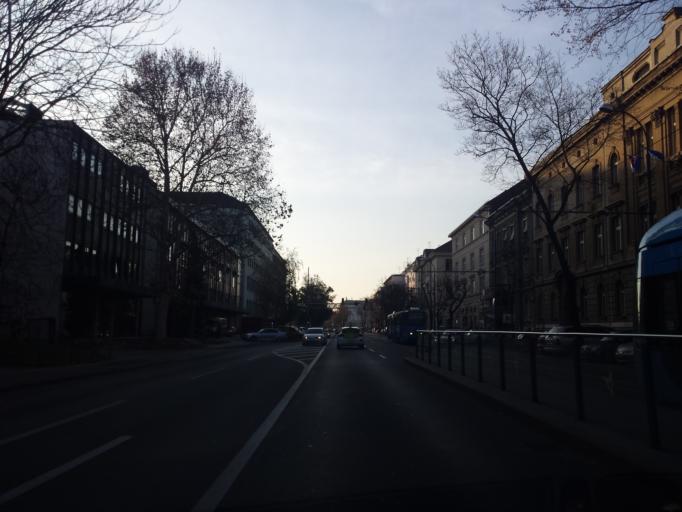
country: HR
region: Grad Zagreb
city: Zagreb - Centar
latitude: 45.8054
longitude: 15.9834
